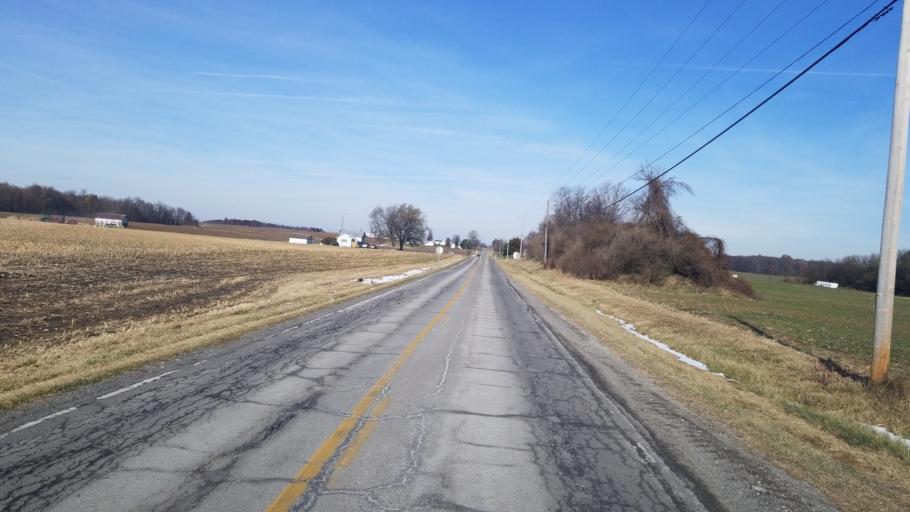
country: US
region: Ohio
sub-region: Huron County
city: Willard
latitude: 41.0548
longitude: -82.6824
